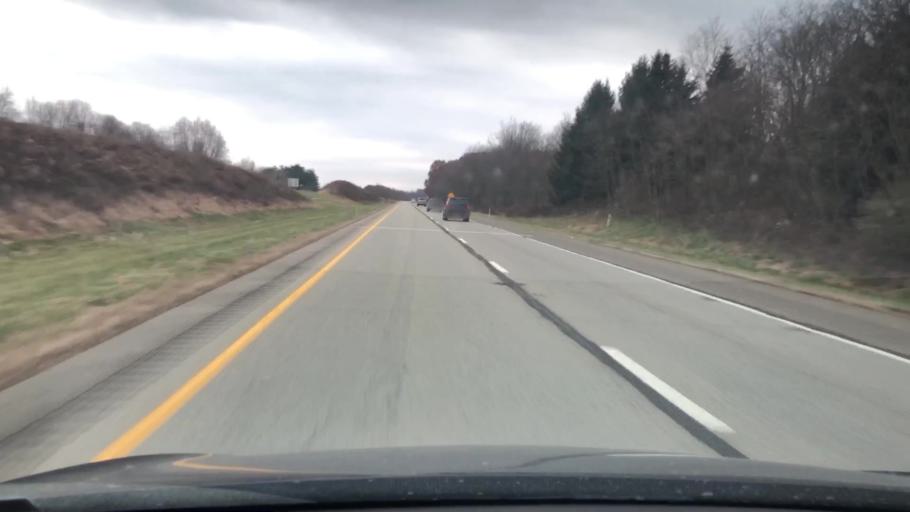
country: US
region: Pennsylvania
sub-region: Armstrong County
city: West Hills
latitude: 40.7906
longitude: -79.5769
